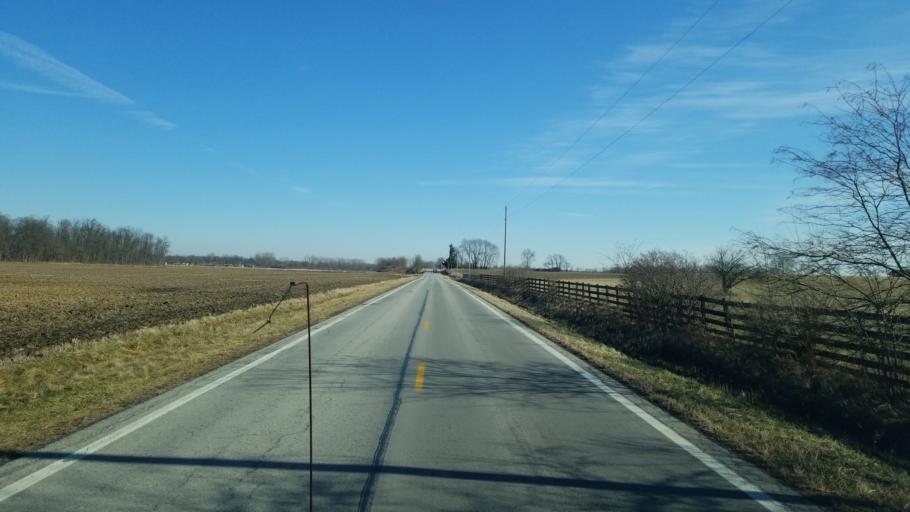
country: US
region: Ohio
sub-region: Henry County
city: Liberty Center
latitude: 41.4151
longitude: -83.9612
